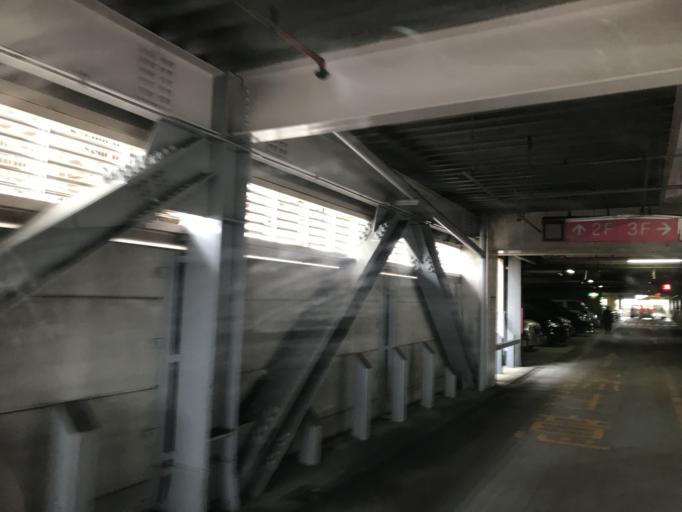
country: JP
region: Aichi
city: Kasugai
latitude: 35.2380
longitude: 136.9614
